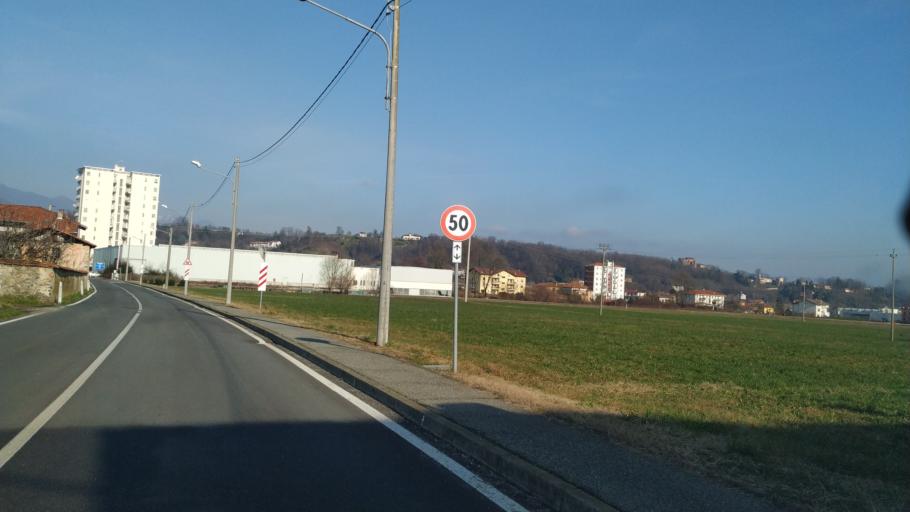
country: IT
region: Piedmont
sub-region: Provincia di Biella
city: Valdengo
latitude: 45.5606
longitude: 8.1386
